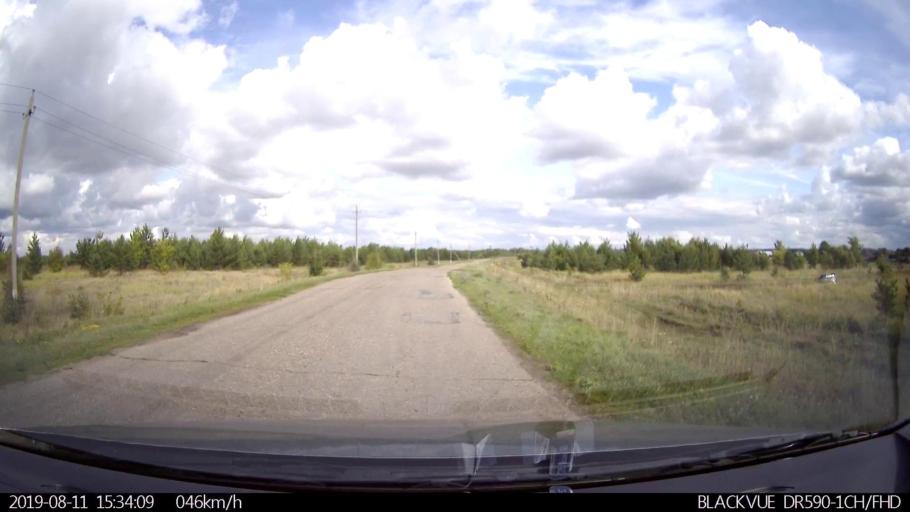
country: RU
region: Ulyanovsk
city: Ignatovka
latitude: 53.8620
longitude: 47.5918
